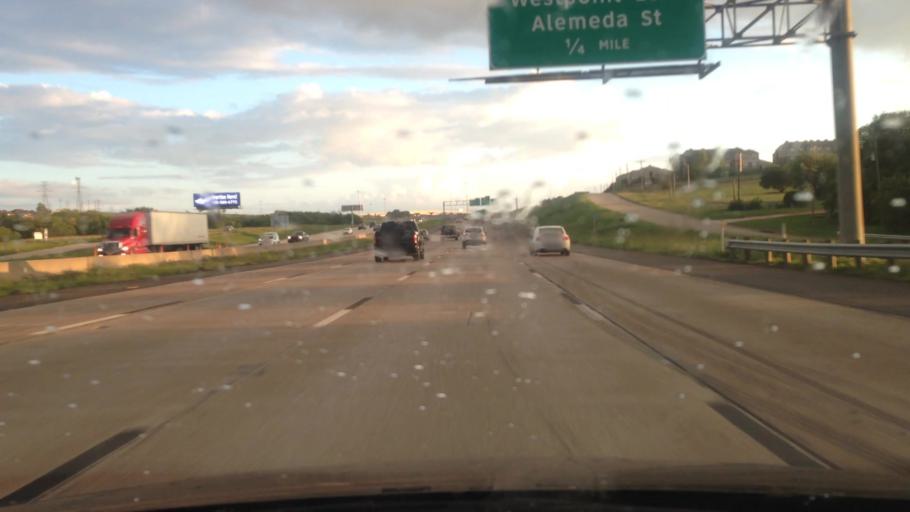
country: US
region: Texas
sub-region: Tarrant County
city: White Settlement
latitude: 32.7513
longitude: -97.4806
